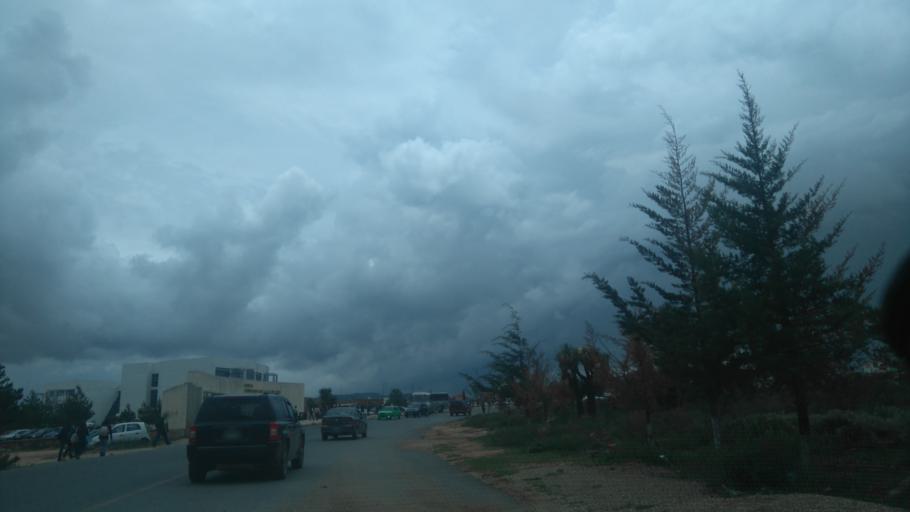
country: MX
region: Zacatecas
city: Zacatecas
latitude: 22.7700
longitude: -102.6434
